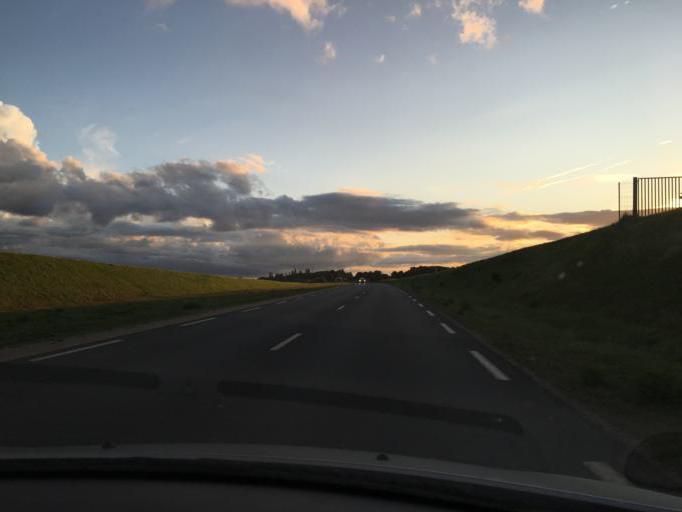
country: FR
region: Centre
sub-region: Departement d'Eure-et-Loir
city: Chateaudun
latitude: 48.0854
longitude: 1.3203
